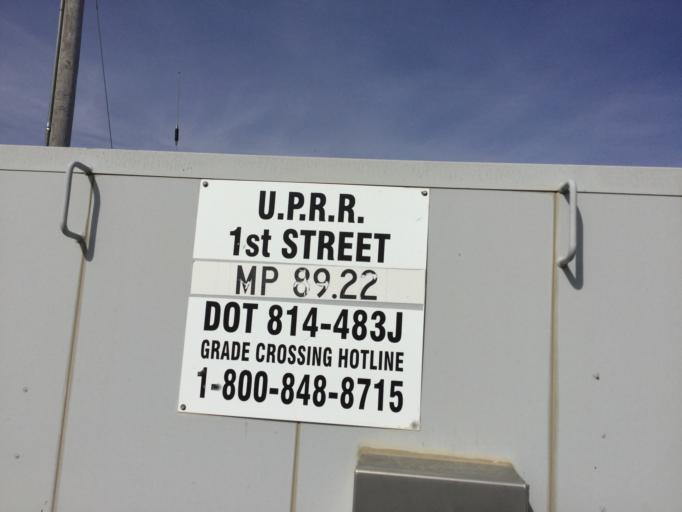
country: US
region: Kansas
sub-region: Nemaha County
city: Seneca
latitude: 39.8745
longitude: -96.2631
